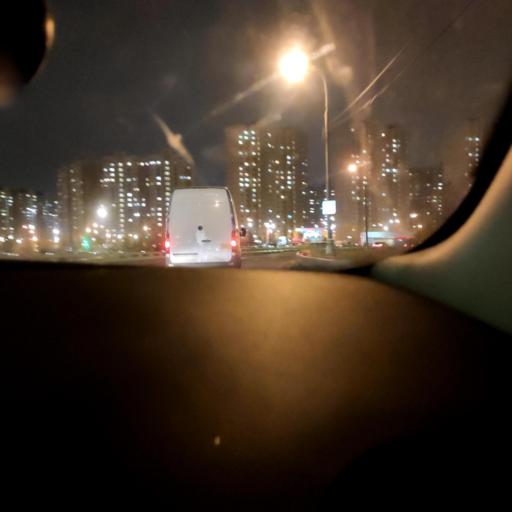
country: RU
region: Moscow
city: Nekrasovka
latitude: 55.7087
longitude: 37.9222
